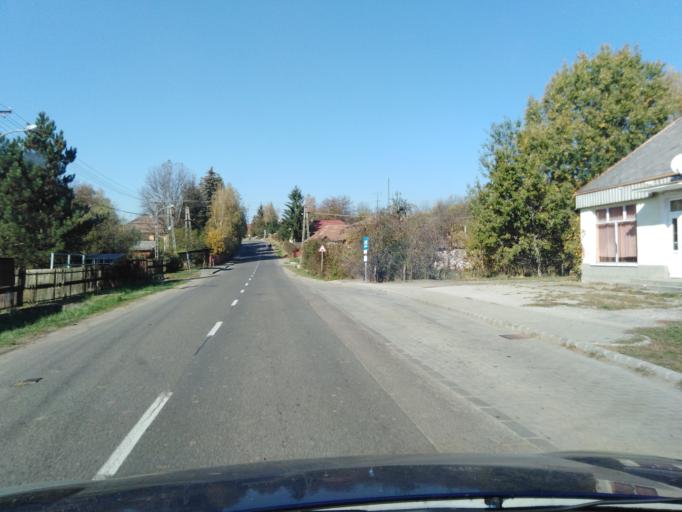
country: HU
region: Nograd
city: Karancskeszi
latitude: 48.1605
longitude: 19.7087
